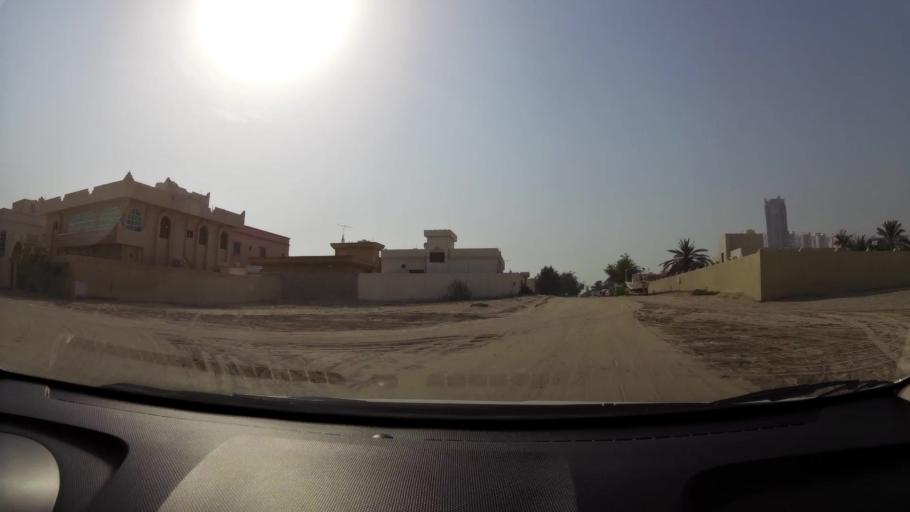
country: AE
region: Ajman
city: Ajman
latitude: 25.3859
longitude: 55.4326
